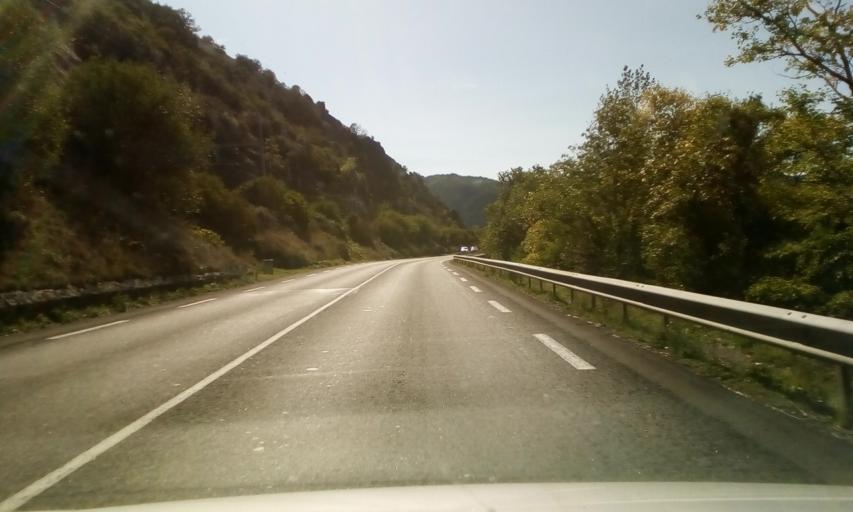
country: FR
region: Rhone-Alpes
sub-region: Departement de l'Ardeche
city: Saint-Jean-de-Muzols
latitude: 45.0867
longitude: 4.8330
